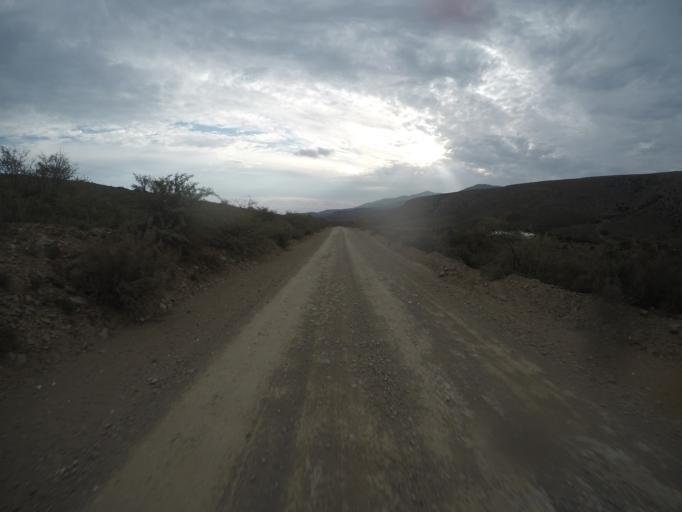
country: ZA
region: Eastern Cape
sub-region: Cacadu District Municipality
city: Willowmore
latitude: -33.4870
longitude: 23.5500
